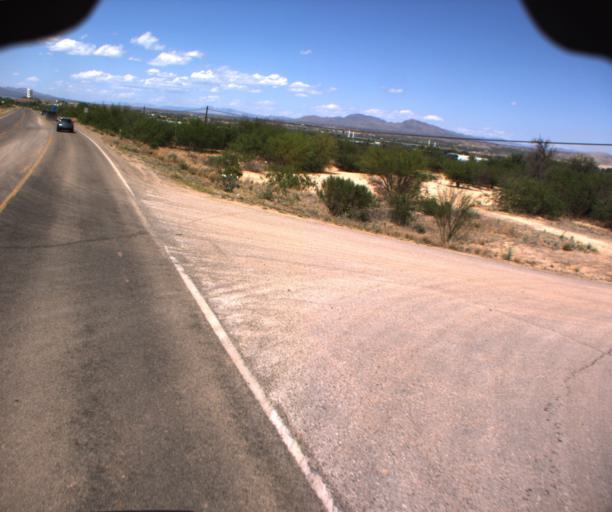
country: US
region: Arizona
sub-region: Cochise County
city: Benson
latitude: 31.9552
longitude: -110.2862
